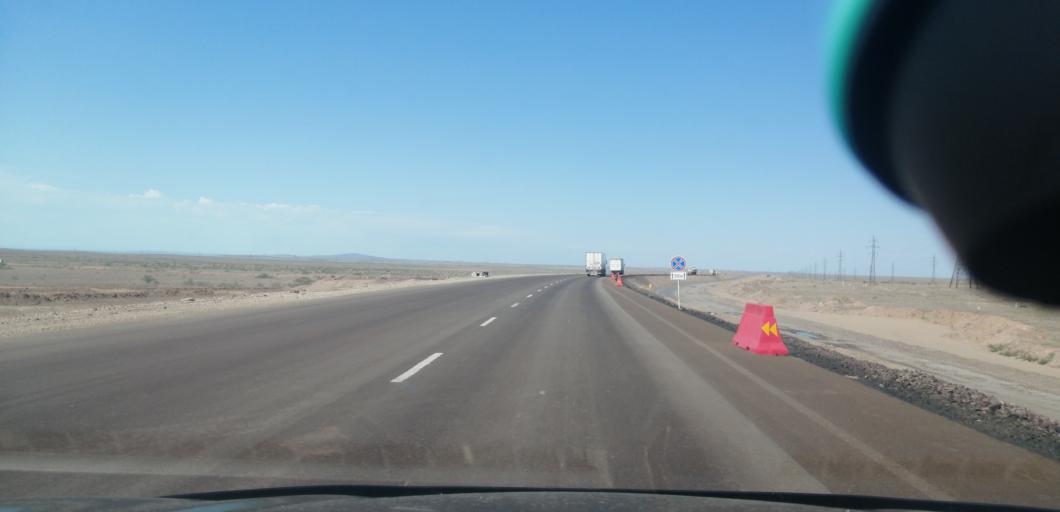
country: KZ
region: Qaraghandy
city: Balqash
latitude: 46.8073
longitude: 74.7097
